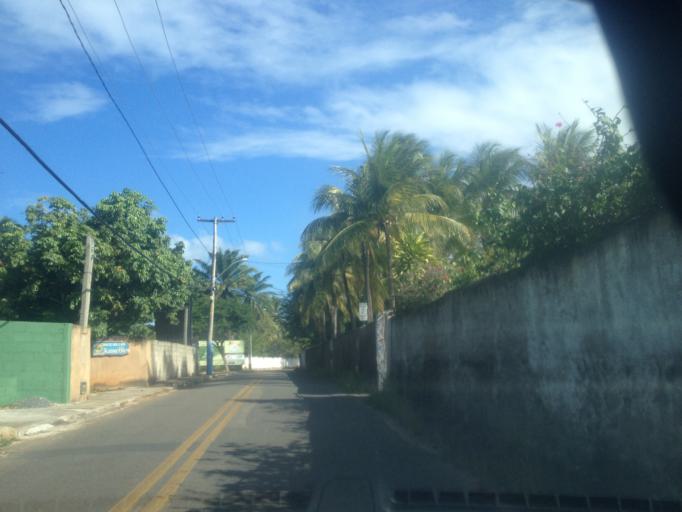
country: BR
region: Bahia
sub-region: Mata De Sao Joao
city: Mata de Sao Joao
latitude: -12.6166
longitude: -38.0439
